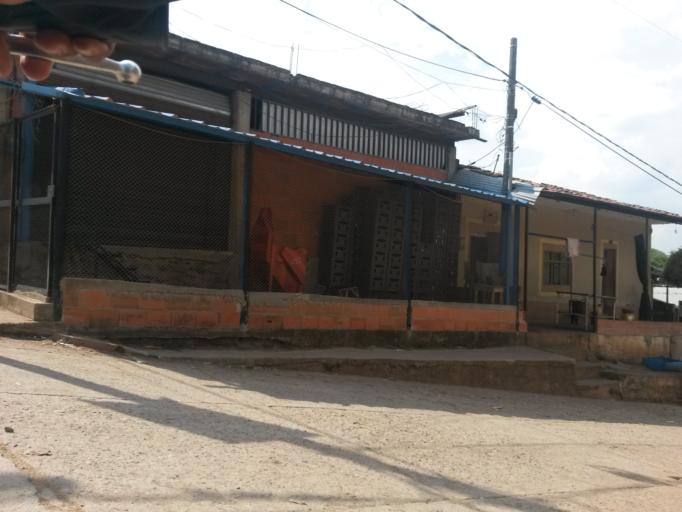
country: CO
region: Cauca
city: Buenos Aires
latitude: 3.0167
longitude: -76.6415
